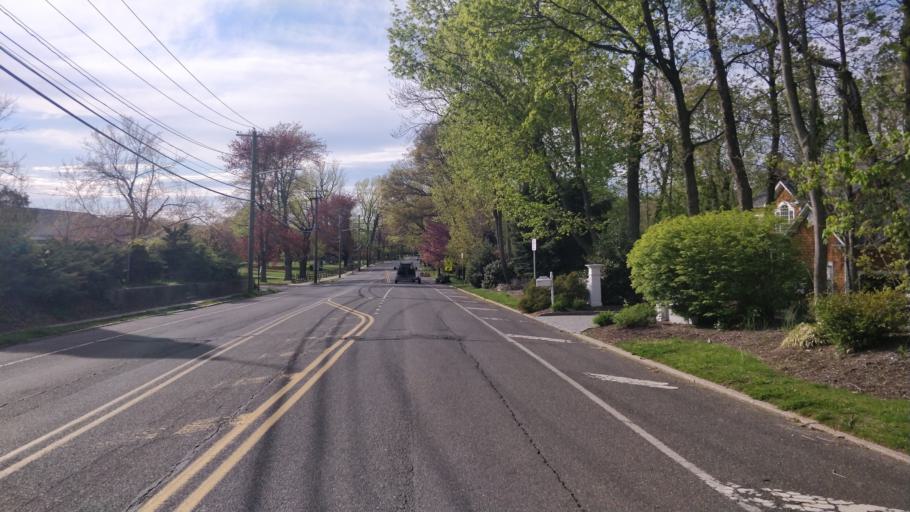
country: US
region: New York
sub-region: Suffolk County
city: East Setauket
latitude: 40.9432
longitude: -73.1078
